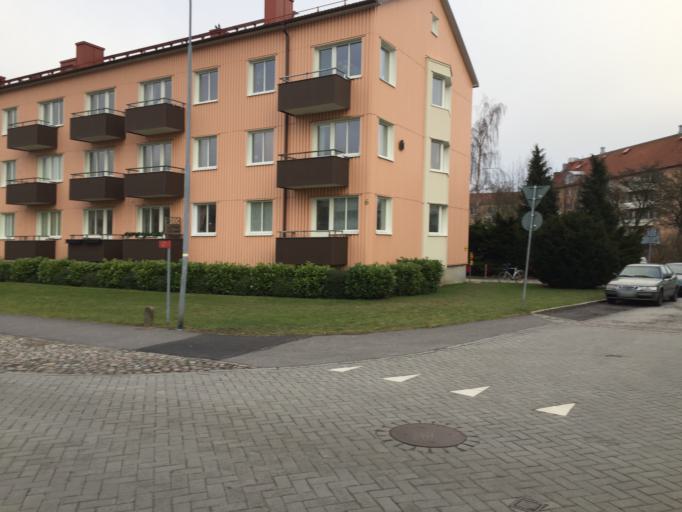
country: SE
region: Skane
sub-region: Svedala Kommun
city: Svedala
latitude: 55.5100
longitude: 13.2329
